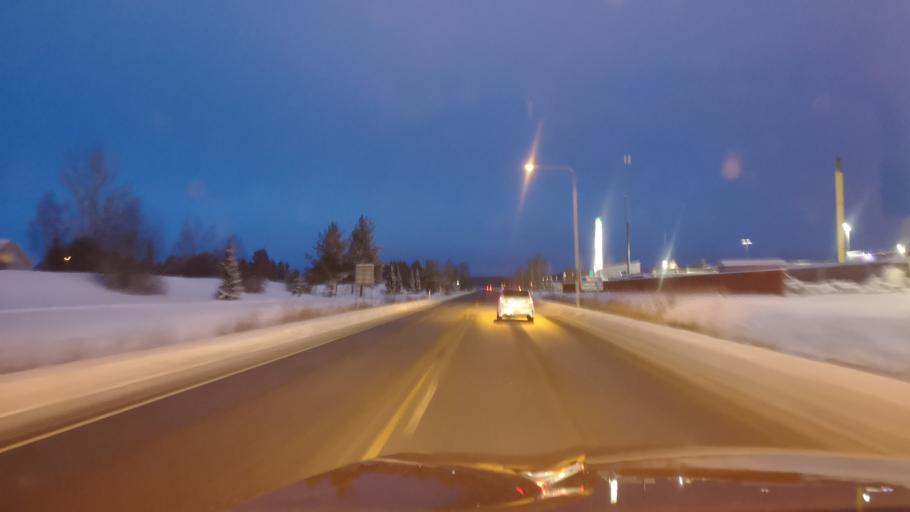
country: FI
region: Varsinais-Suomi
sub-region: Loimaa
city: Loimaa
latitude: 60.8553
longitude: 23.0406
